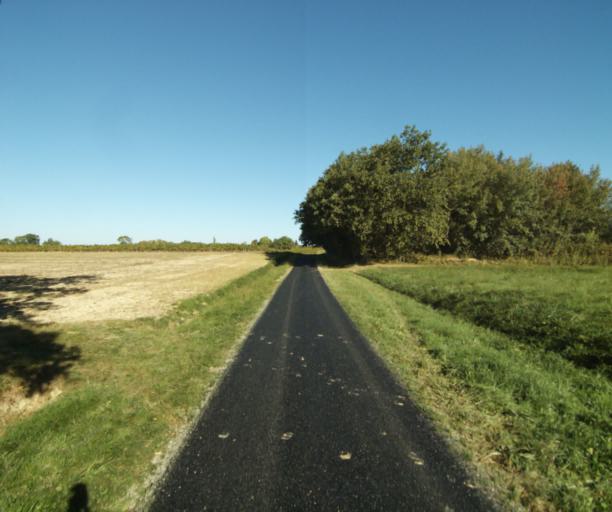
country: FR
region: Midi-Pyrenees
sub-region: Departement du Gers
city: Gondrin
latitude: 43.8114
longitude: 0.1954
